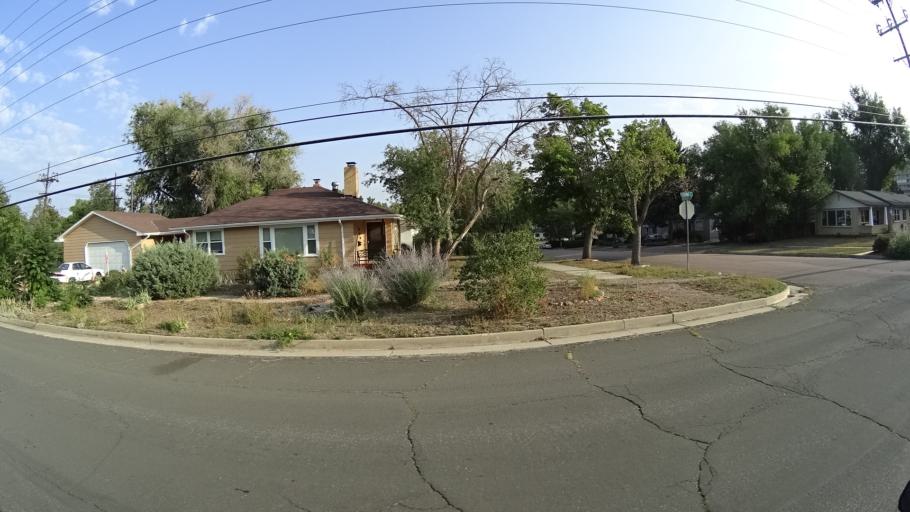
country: US
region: Colorado
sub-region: El Paso County
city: Colorado Springs
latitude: 38.8345
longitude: -104.7979
